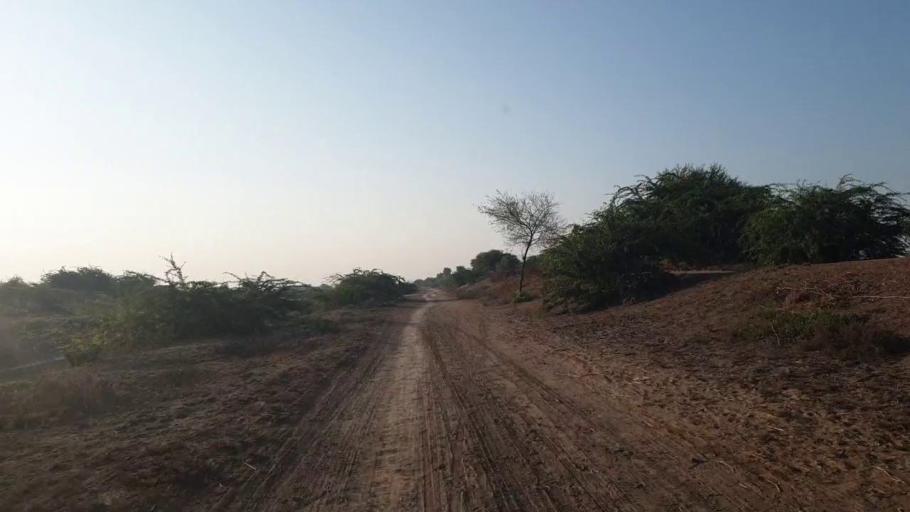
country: PK
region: Sindh
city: Badin
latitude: 24.6418
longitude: 68.7911
